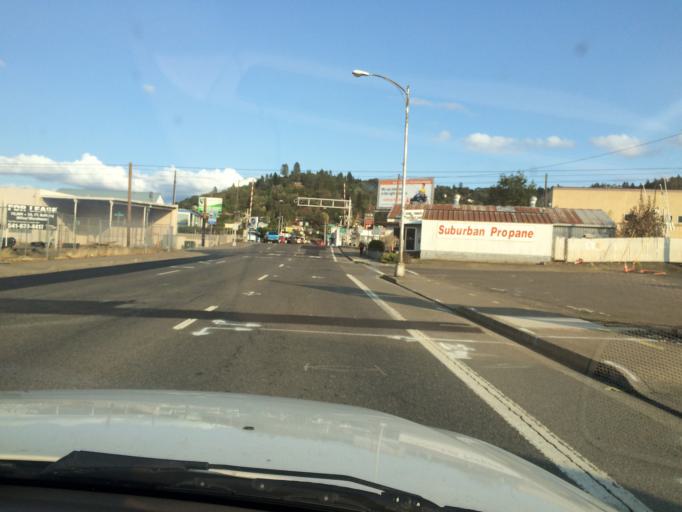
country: US
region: Oregon
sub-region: Douglas County
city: Roseburg
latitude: 43.2106
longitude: -123.3487
